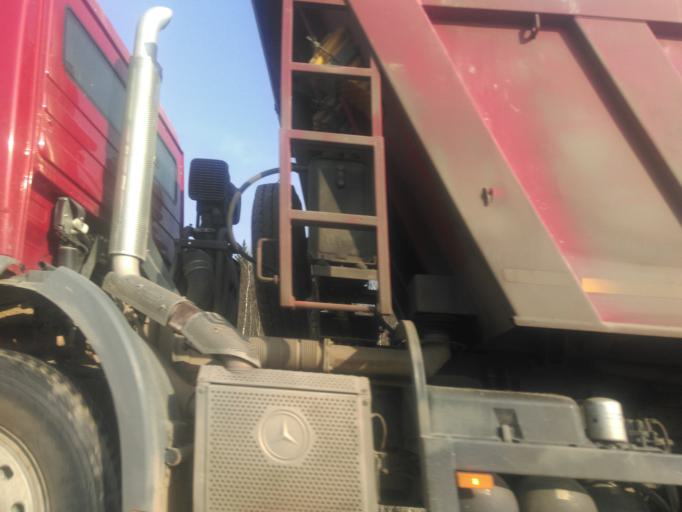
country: RU
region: Moskovskaya
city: Golitsyno
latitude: 55.5984
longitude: 36.9637
